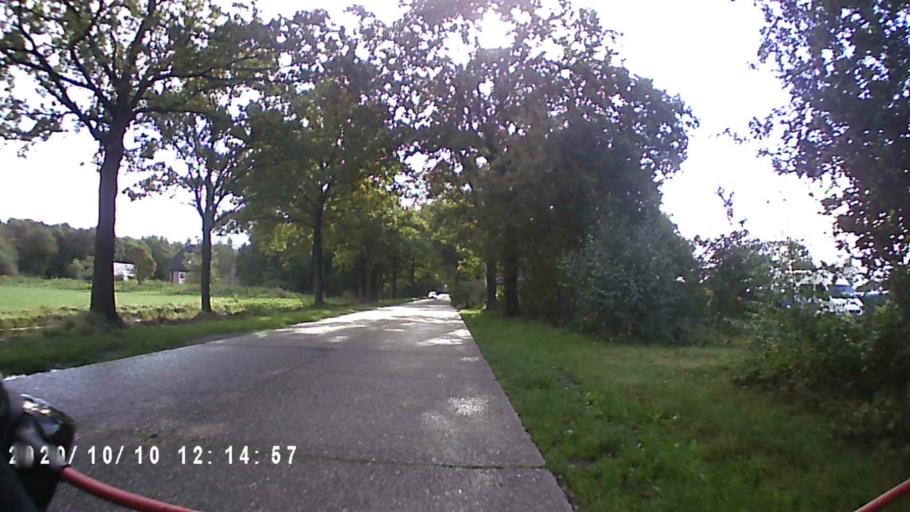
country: NL
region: Friesland
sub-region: Gemeente Heerenveen
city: Jubbega
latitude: 53.0281
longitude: 6.1618
